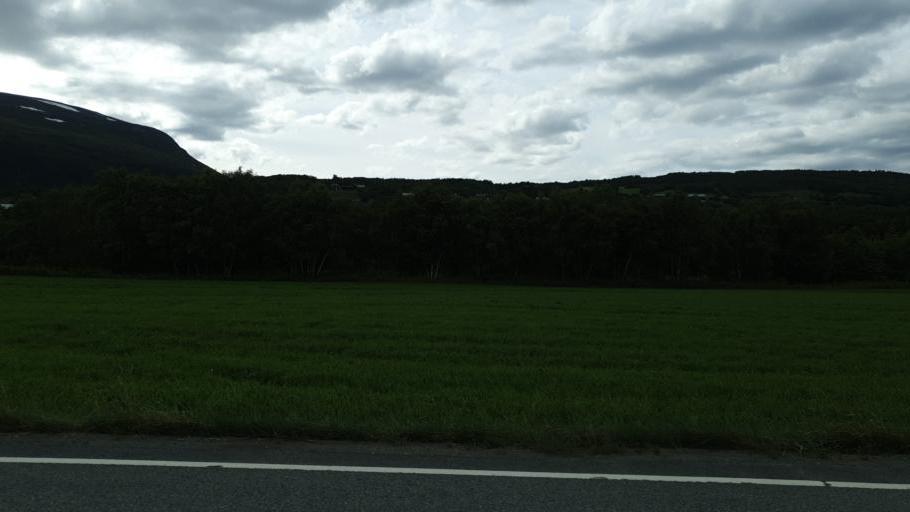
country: NO
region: Sor-Trondelag
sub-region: Oppdal
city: Oppdal
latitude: 62.5589
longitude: 9.6374
